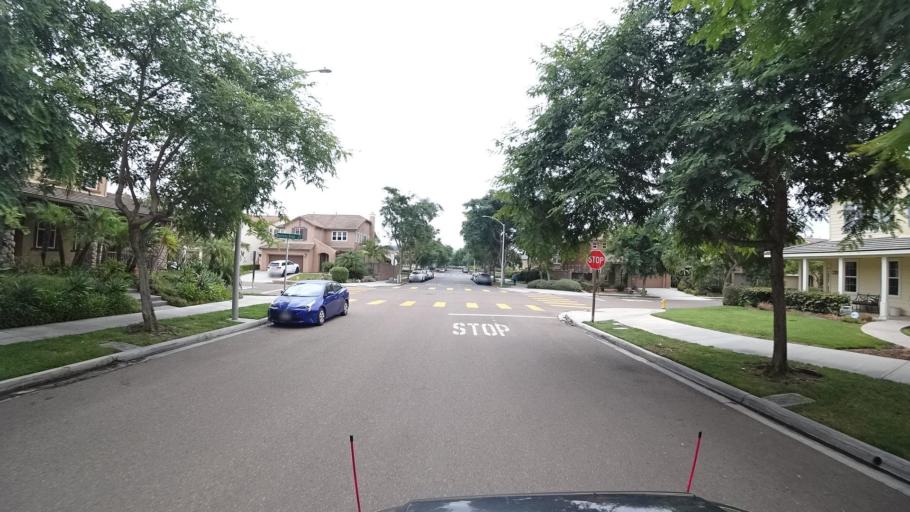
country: US
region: California
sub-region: San Diego County
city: Fairbanks Ranch
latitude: 33.0284
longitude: -117.1104
